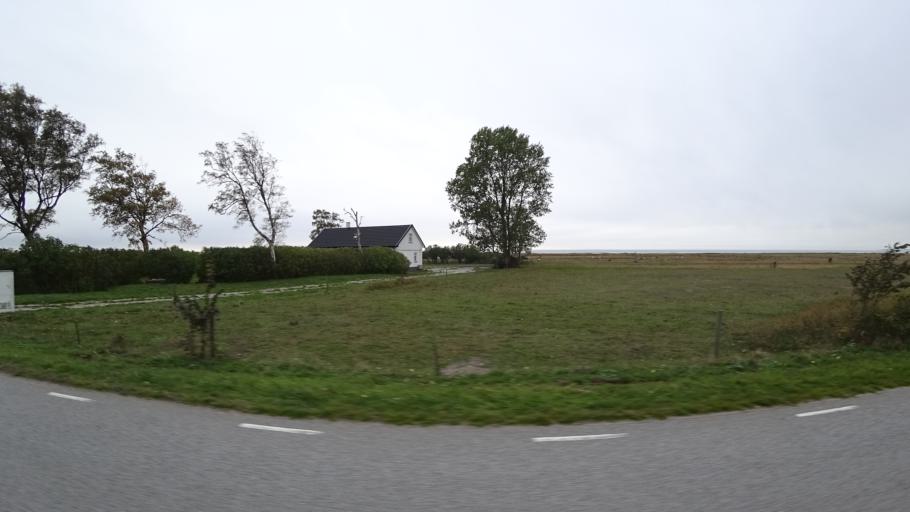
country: SE
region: Skane
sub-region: Kavlinge Kommun
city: Hofterup
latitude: 55.8147
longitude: 12.9352
